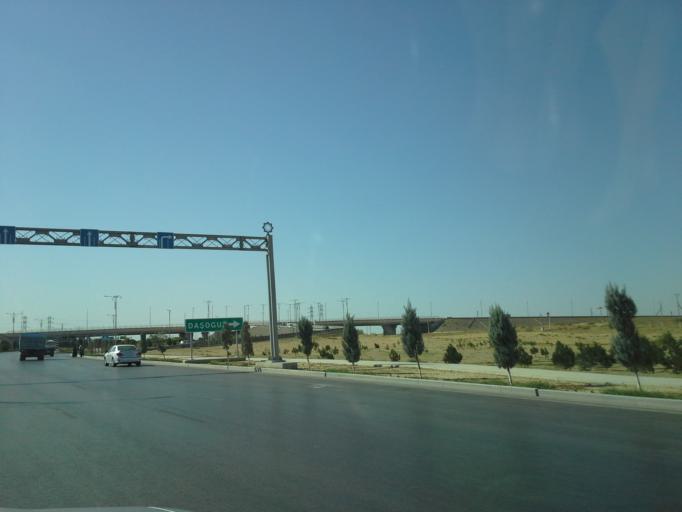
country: TM
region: Ahal
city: Annau
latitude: 37.9117
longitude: 58.4899
